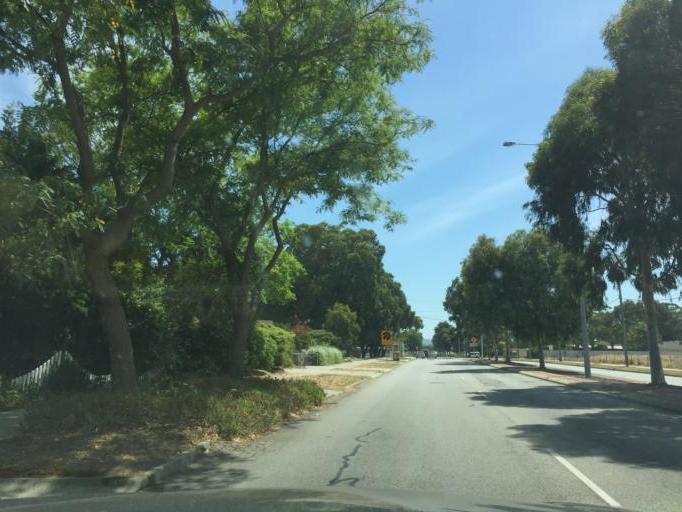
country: AU
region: Western Australia
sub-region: Gosnells
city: Thornlie
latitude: -32.0764
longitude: 115.9596
